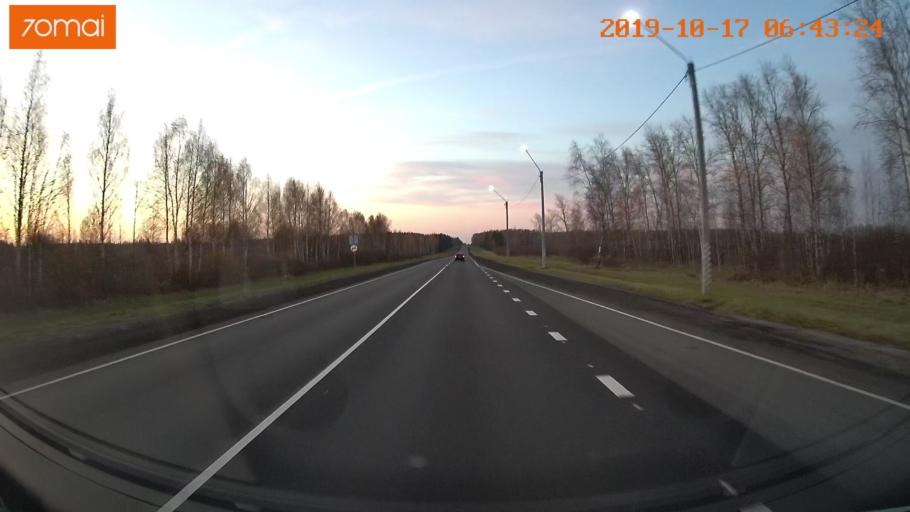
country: RU
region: Vladimir
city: Kideksha
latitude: 56.5879
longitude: 40.5552
